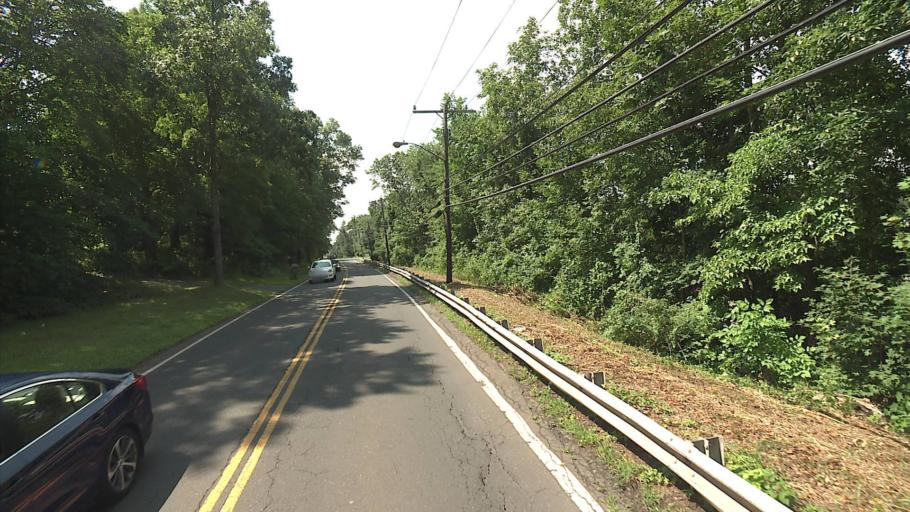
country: US
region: Connecticut
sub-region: Middlesex County
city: Cromwell
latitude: 41.5924
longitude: -72.6984
